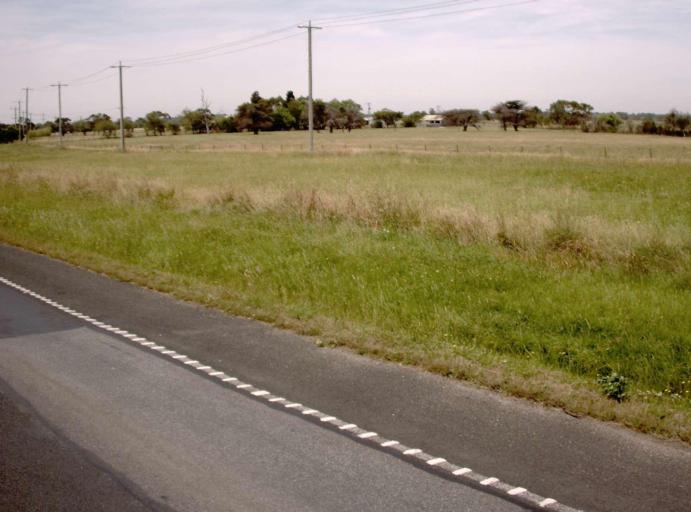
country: AU
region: Victoria
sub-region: Mornington Peninsula
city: Langwarrin South
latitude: -38.2125
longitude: 145.2184
